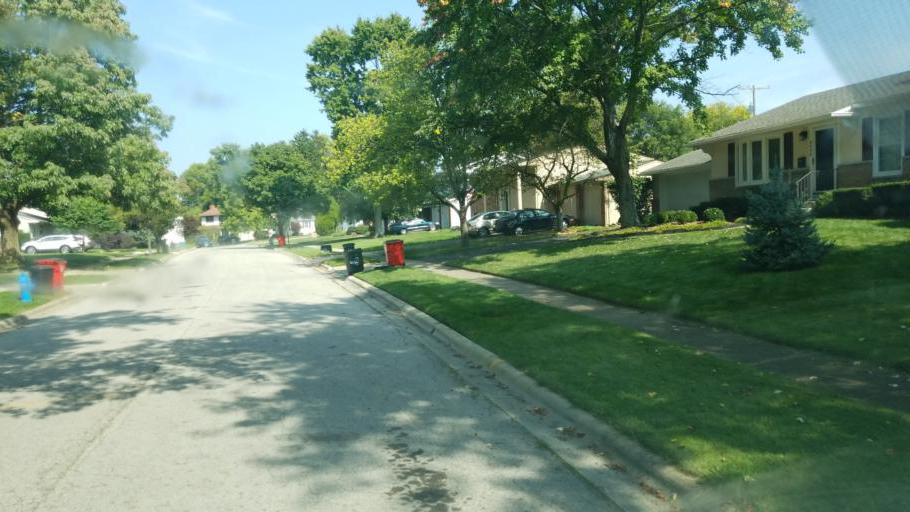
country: US
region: Ohio
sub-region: Franklin County
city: Worthington
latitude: 40.1008
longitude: -83.0203
